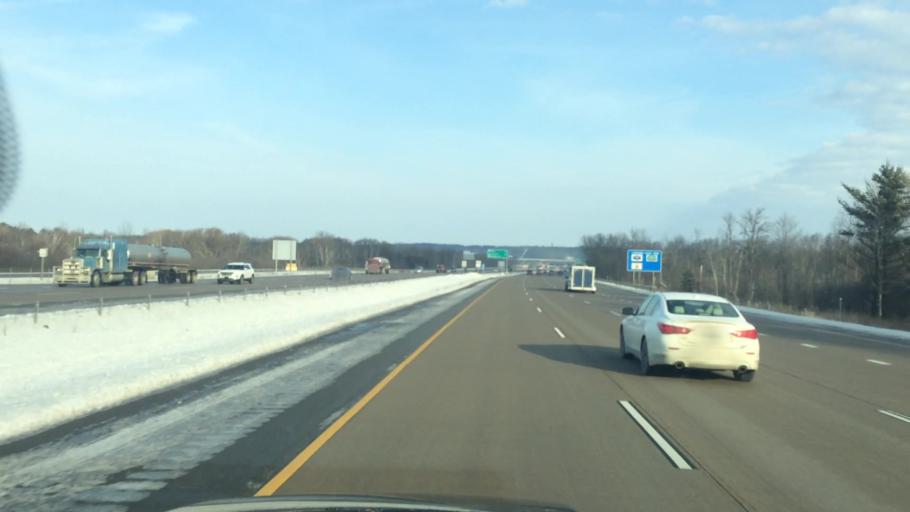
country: US
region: Wisconsin
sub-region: Marathon County
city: Rib Mountain
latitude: 44.9379
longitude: -89.6658
